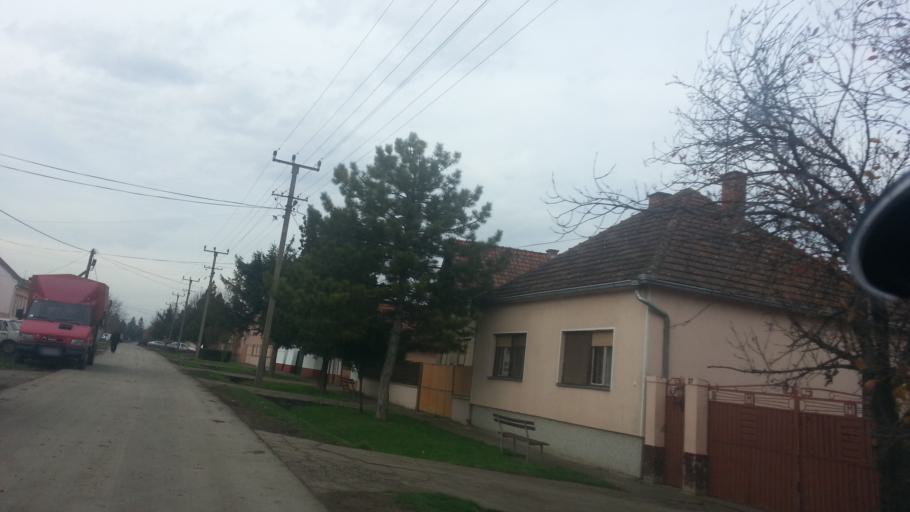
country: RS
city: Putinci
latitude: 44.9636
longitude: 19.9799
